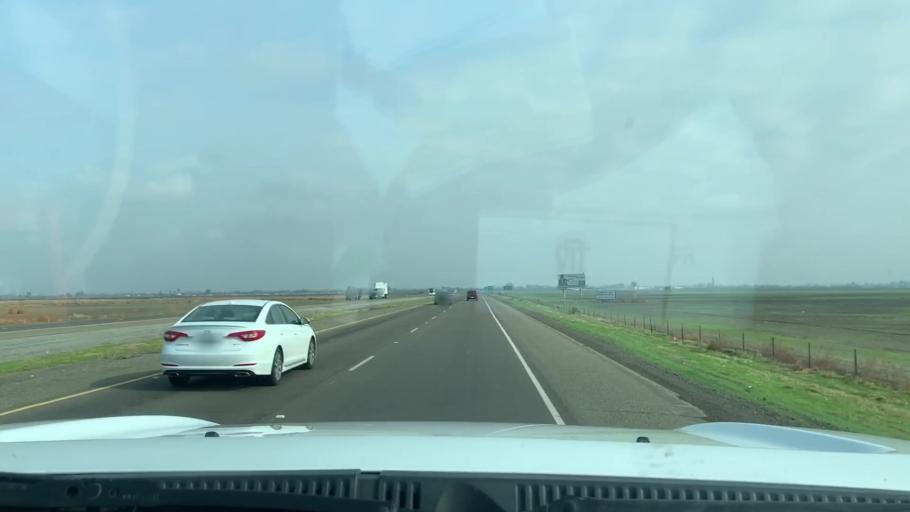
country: US
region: California
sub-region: Kings County
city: Lemoore
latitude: 36.2737
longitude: -119.8267
